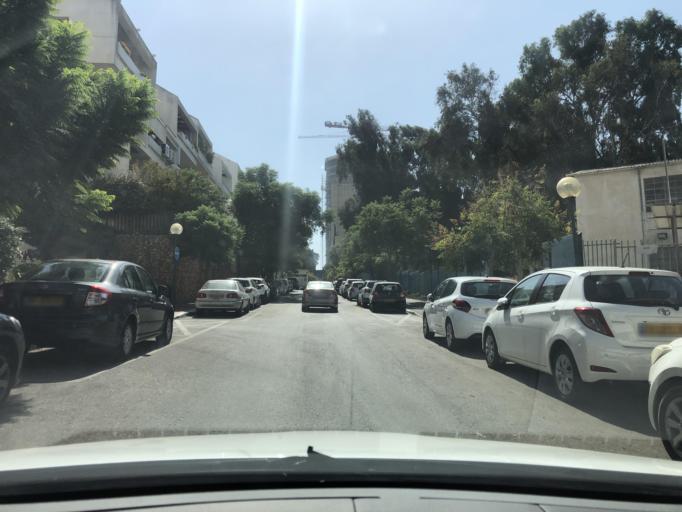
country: IL
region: Central District
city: Kfar Saba
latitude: 32.1759
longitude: 34.8940
